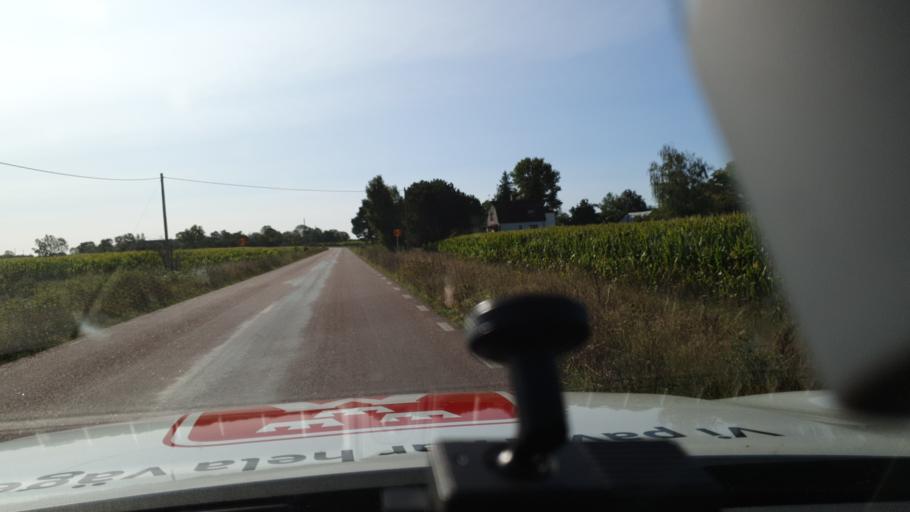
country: SE
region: Gotland
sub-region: Gotland
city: Hemse
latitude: 57.1561
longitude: 18.2811
